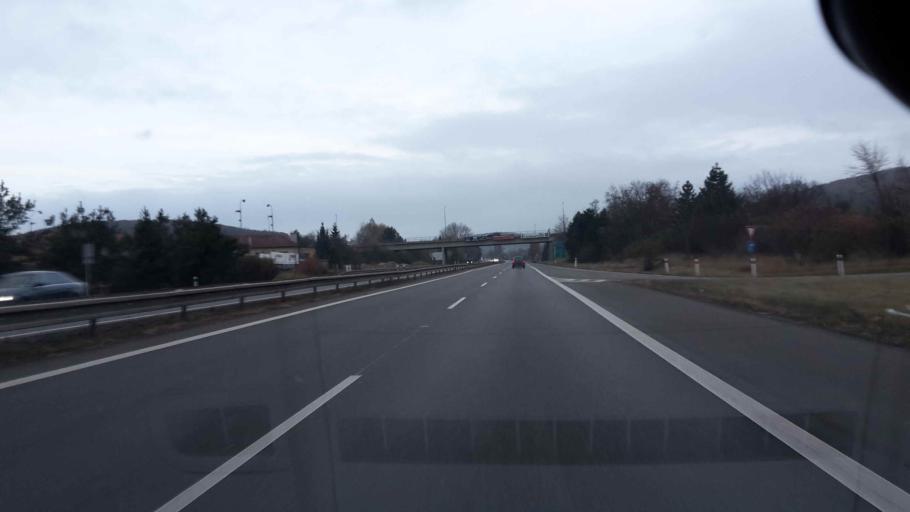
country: CZ
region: South Moravian
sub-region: Okres Brno-Venkov
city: Lelekovice
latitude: 49.2814
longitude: 16.5684
